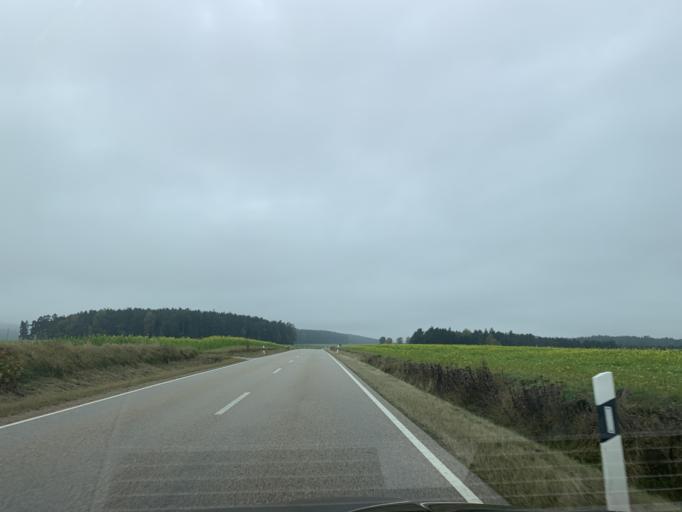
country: DE
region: Bavaria
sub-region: Upper Palatinate
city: Guteneck
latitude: 49.4534
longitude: 12.2438
